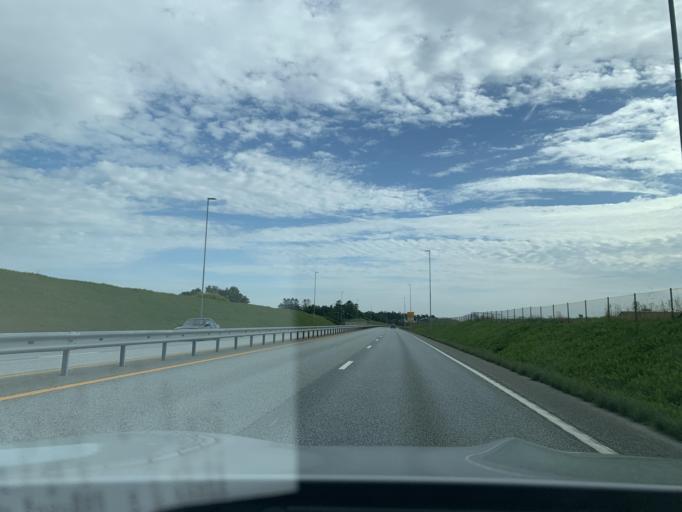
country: NO
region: Rogaland
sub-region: Sandnes
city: Sandnes
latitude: 58.8229
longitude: 5.7023
